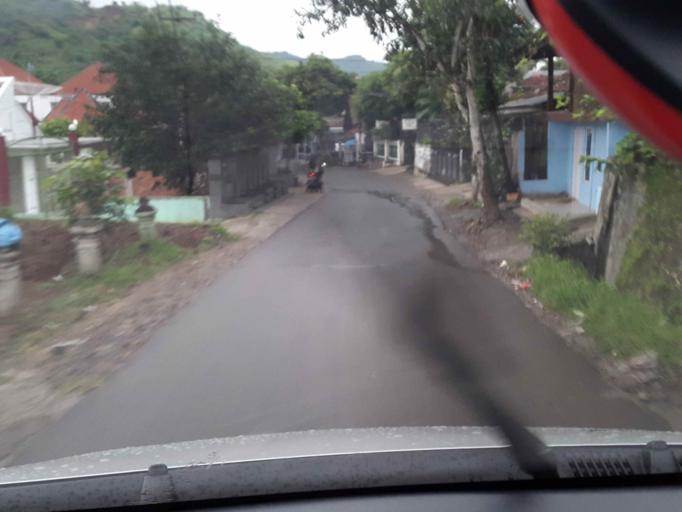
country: ID
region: West Java
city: Sukabumi
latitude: -6.9145
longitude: 106.8604
